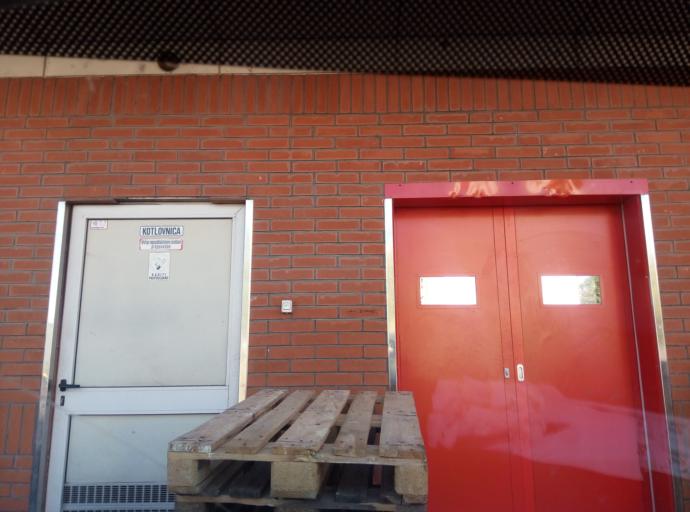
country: SI
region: Ljubljana
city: Ljubljana
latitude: 46.0695
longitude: 14.5479
